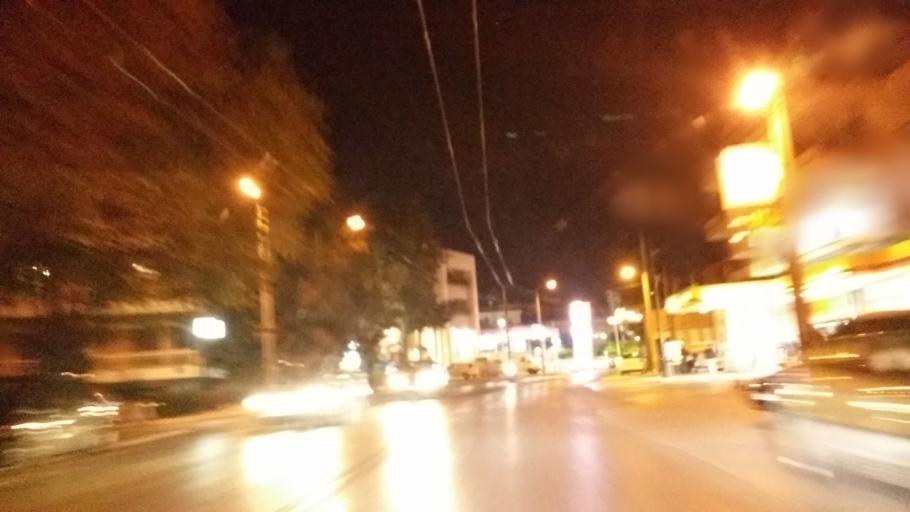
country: GR
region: Attica
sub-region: Nomarchia Athinas
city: Neo Psychiko
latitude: 38.0150
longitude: 23.7903
